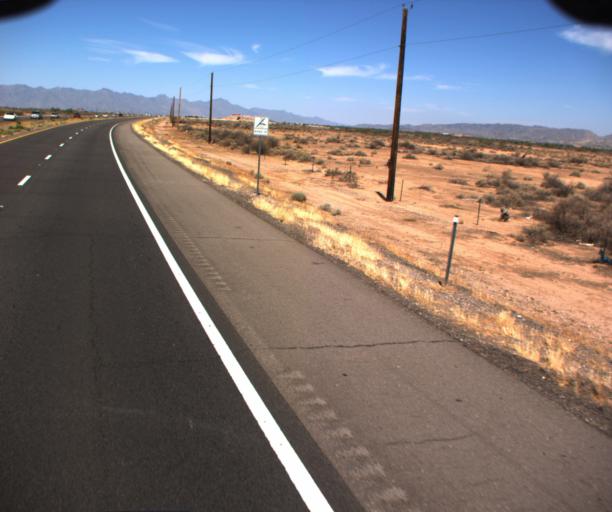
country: US
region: Arizona
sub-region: Maricopa County
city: Sun Lakes
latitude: 33.2523
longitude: -111.9576
